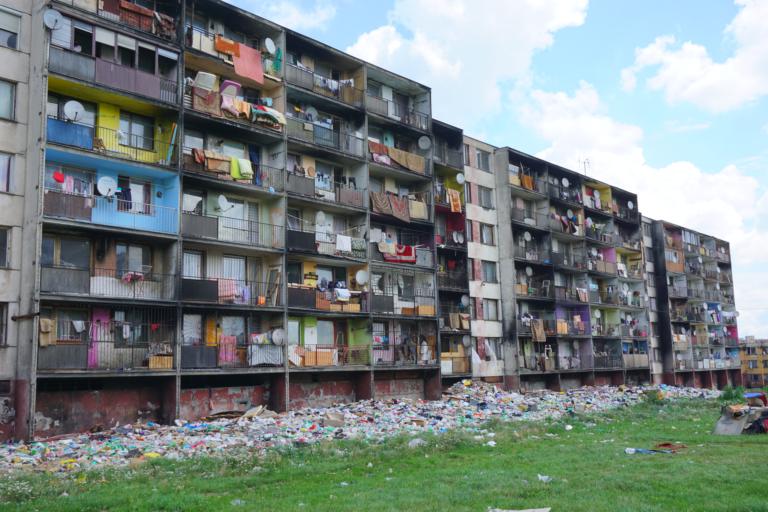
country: SK
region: Kosicky
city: Kosice
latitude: 48.6963
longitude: 21.2211
